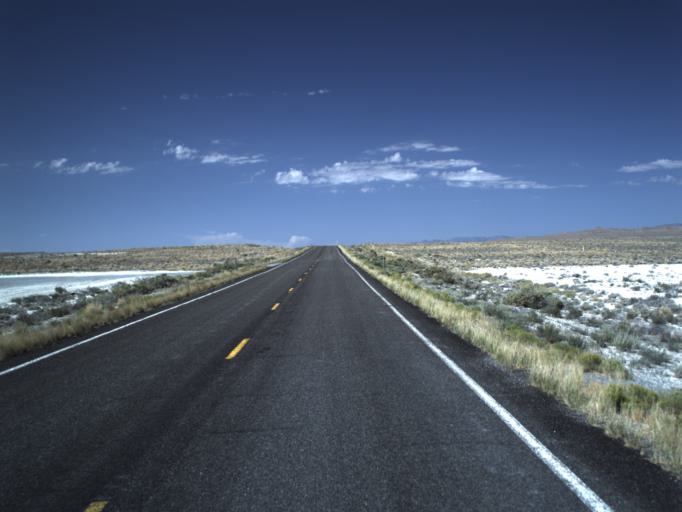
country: US
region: Utah
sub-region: Millard County
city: Delta
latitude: 39.1951
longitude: -112.9924
